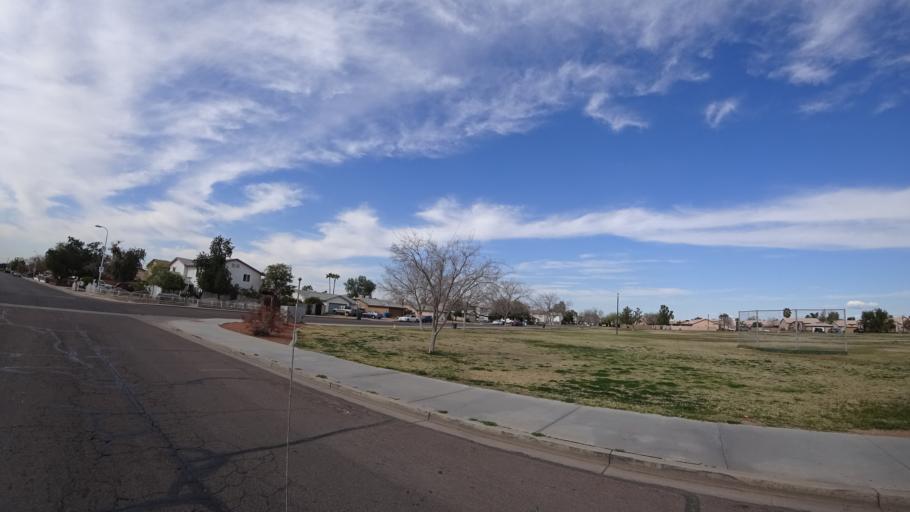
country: US
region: Arizona
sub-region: Maricopa County
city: Tolleson
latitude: 33.4724
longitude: -112.2461
